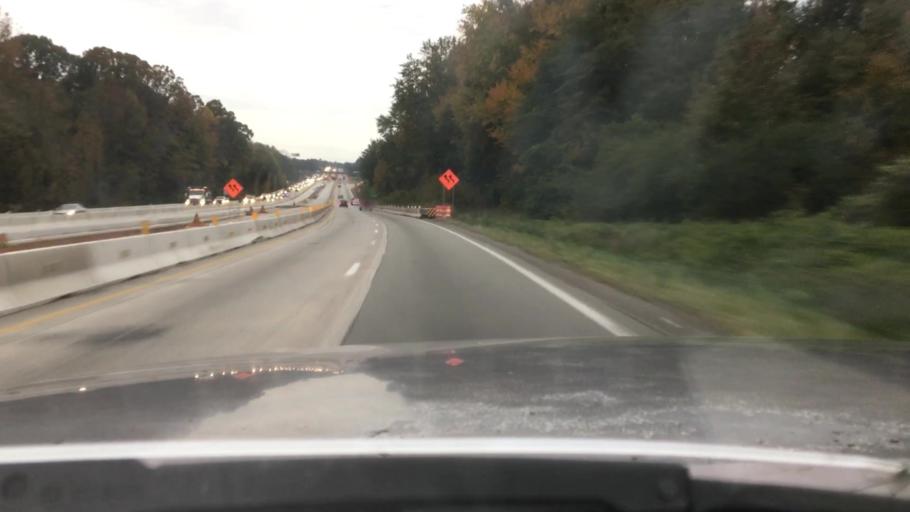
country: US
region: South Carolina
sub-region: Lexington County
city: Lexington
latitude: 33.9866
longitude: -81.1916
